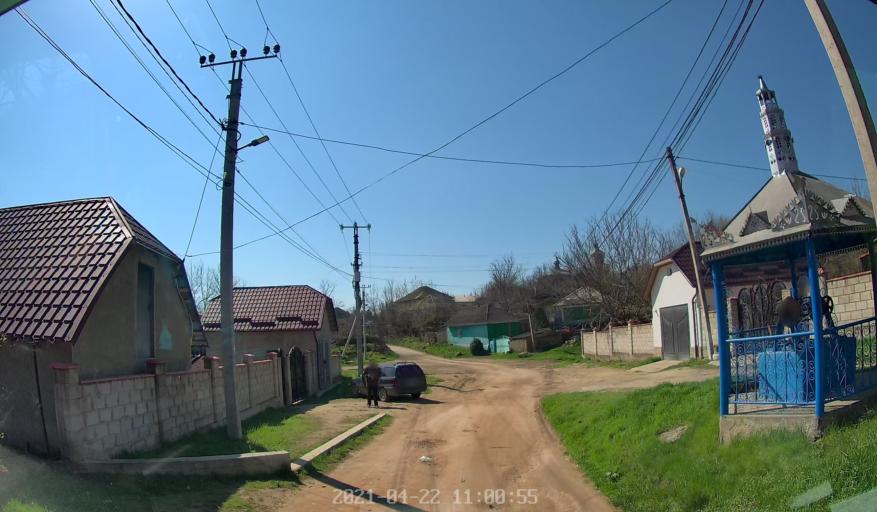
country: MD
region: Chisinau
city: Ciorescu
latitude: 47.1699
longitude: 28.9497
